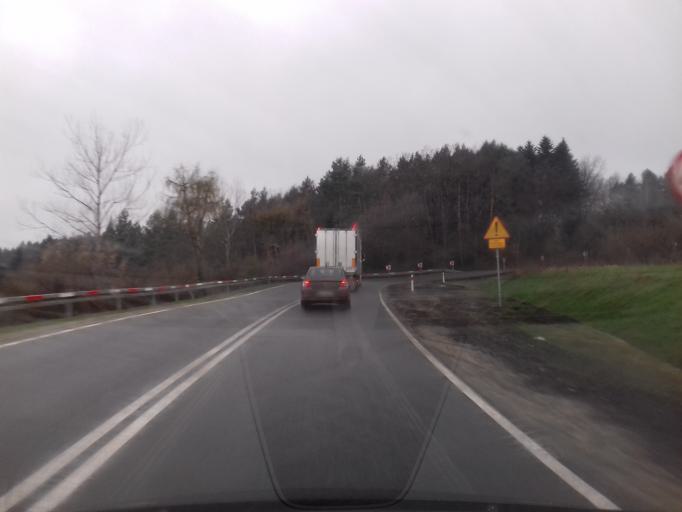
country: PL
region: Lesser Poland Voivodeship
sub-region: Powiat nowosadecki
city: Podegrodzie
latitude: 49.6492
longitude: 20.5939
